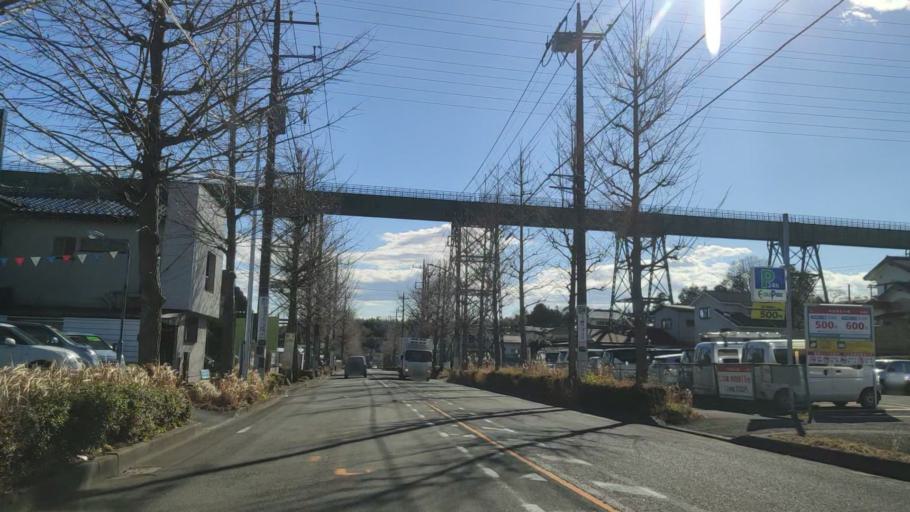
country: JP
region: Kanagawa
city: Minami-rinkan
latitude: 35.5007
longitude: 139.5000
